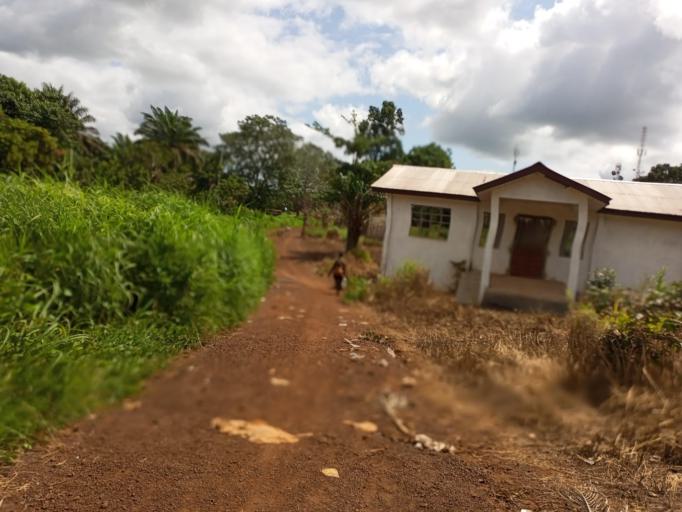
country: SL
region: Northern Province
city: Kamakwie
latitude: 9.4970
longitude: -12.2360
